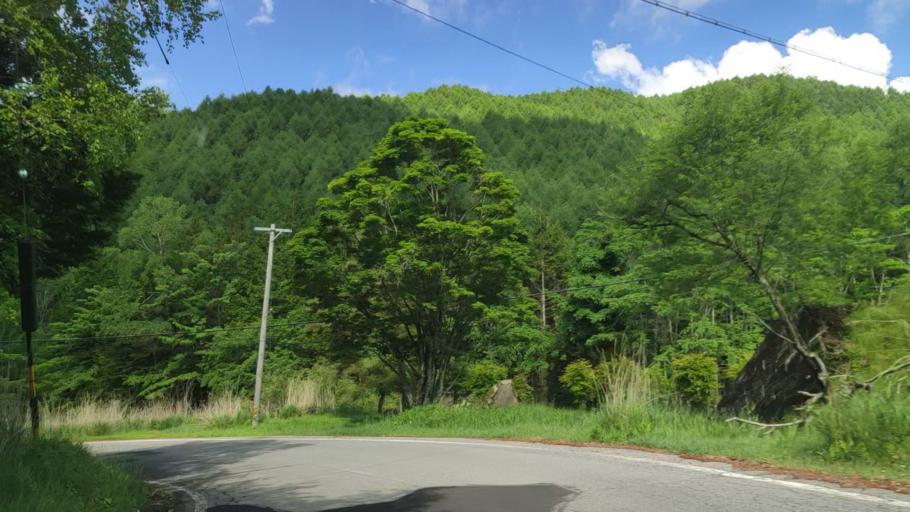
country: JP
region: Nagano
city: Suwa
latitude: 36.0890
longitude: 138.1436
